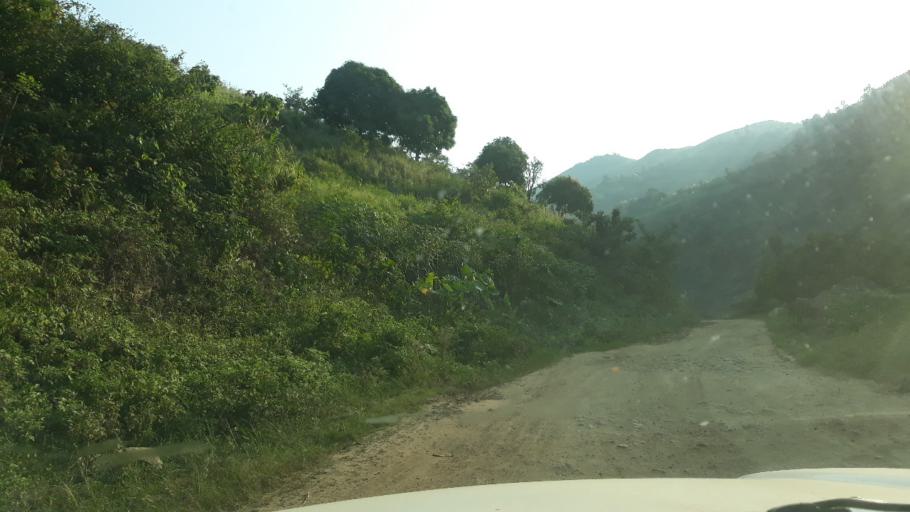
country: RW
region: Western Province
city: Cyangugu
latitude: -2.7140
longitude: 28.9489
